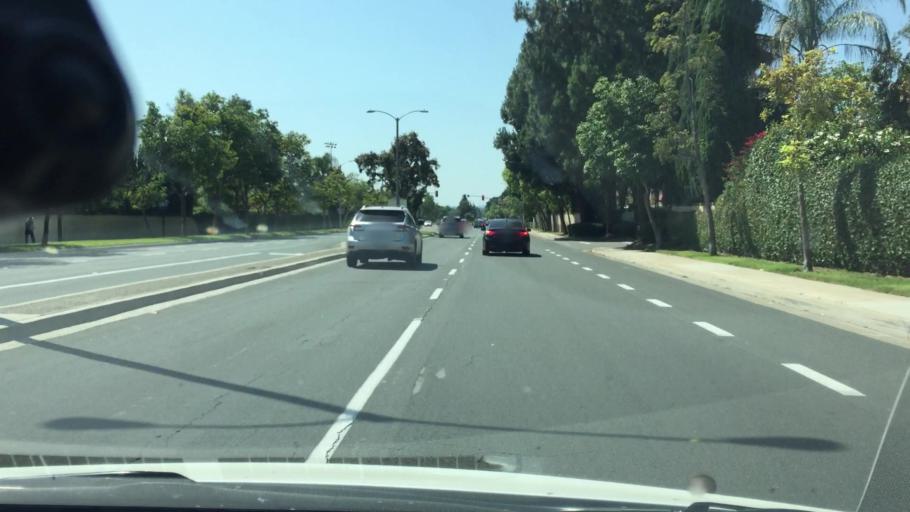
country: US
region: California
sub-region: Orange County
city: North Tustin
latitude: 33.7149
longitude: -117.7748
